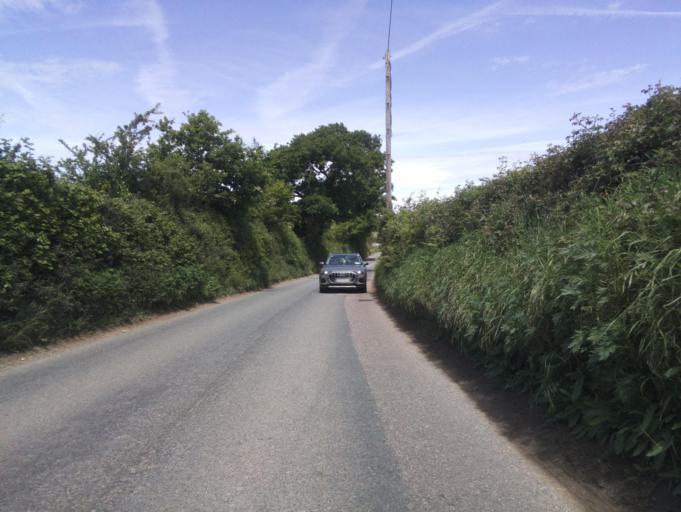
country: GB
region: England
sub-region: Devon
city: Uffculme
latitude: 50.8360
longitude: -3.3031
